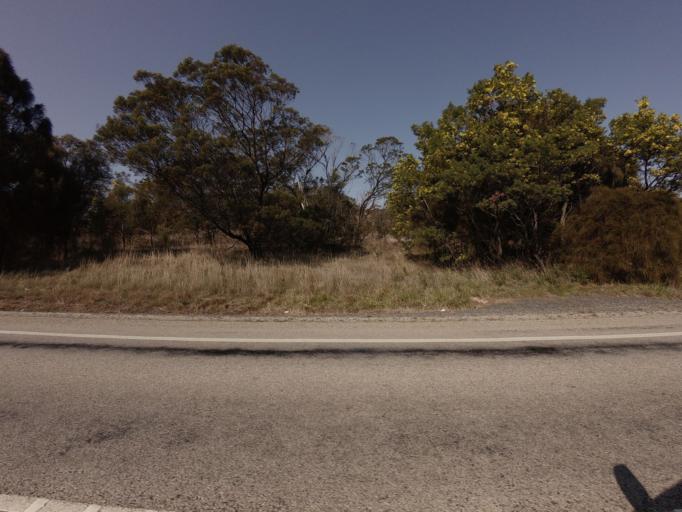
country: AU
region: Tasmania
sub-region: Northern Midlands
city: Evandale
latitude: -41.8190
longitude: 147.5377
